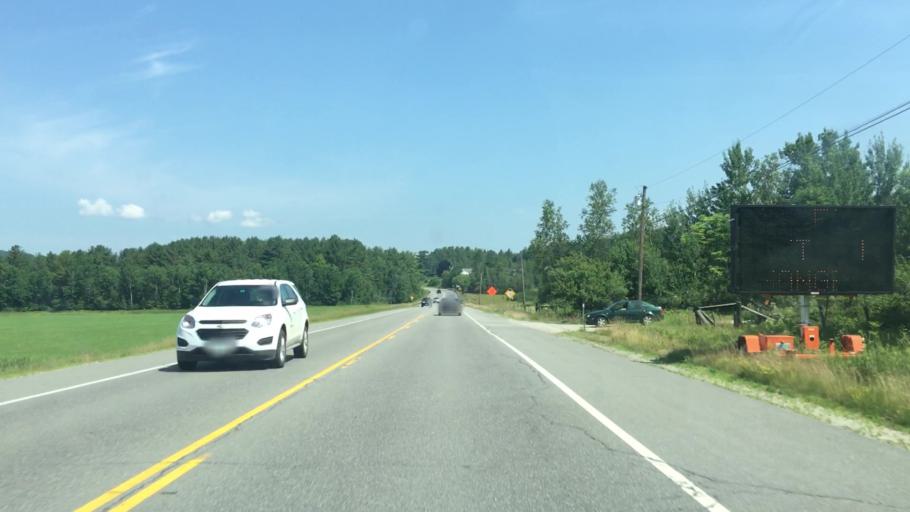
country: US
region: New Hampshire
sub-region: Sullivan County
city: Sunapee
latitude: 43.3648
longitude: -72.1207
